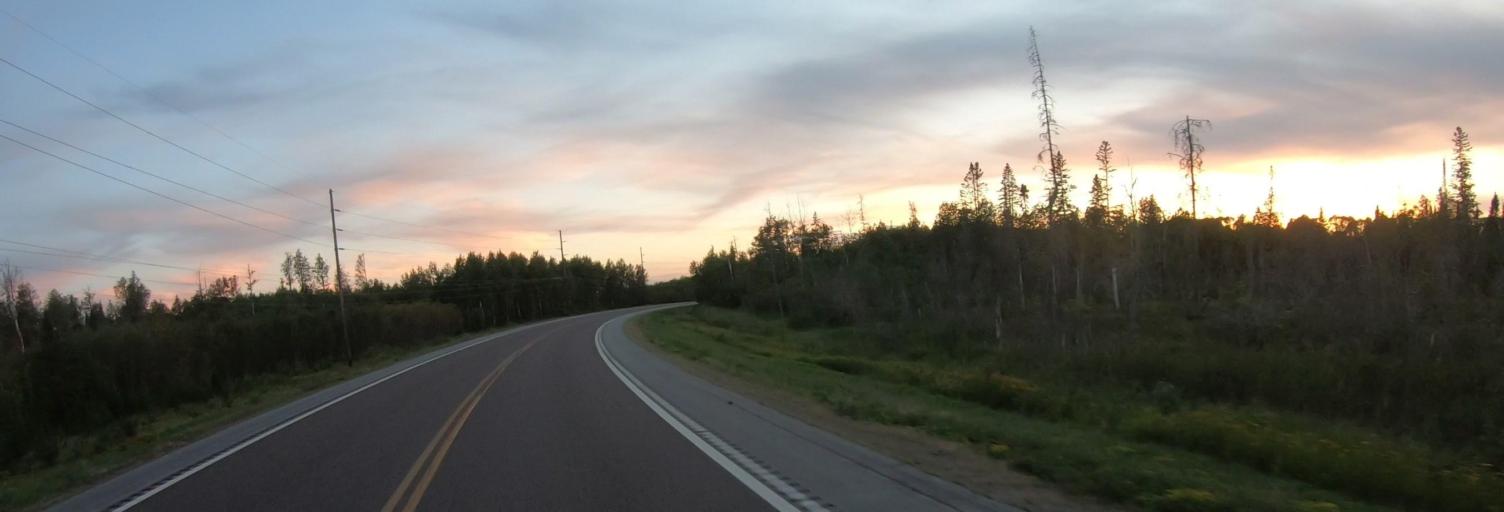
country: US
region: Minnesota
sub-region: Saint Louis County
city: Virginia
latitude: 47.8563
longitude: -92.4670
